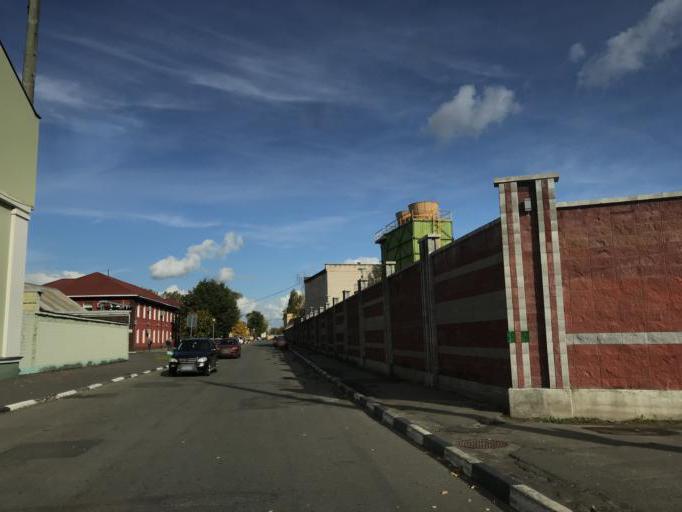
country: BY
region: Gomel
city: Gomel
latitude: 52.4475
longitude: 30.9709
